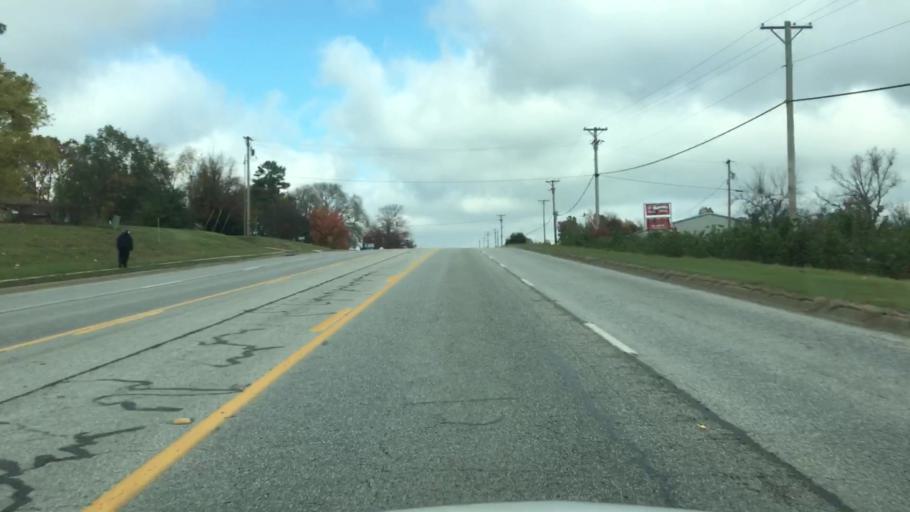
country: US
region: Arkansas
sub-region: Benton County
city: Gentry
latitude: 36.2541
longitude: -94.4852
